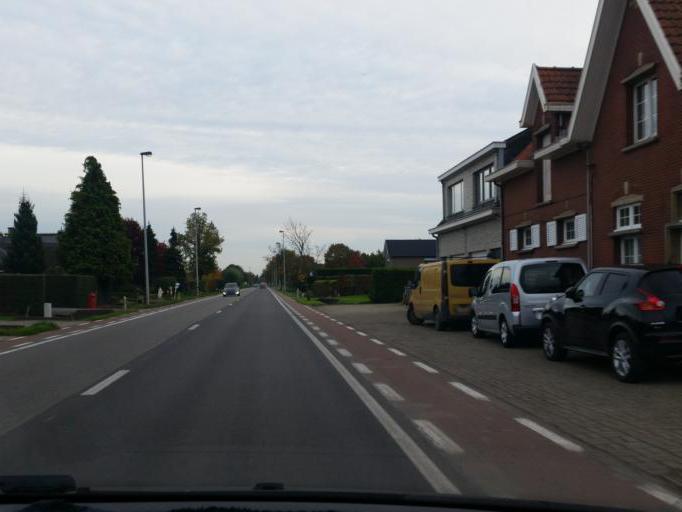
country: BE
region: Flanders
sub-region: Provincie Antwerpen
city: Lier
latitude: 51.1156
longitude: 4.5864
